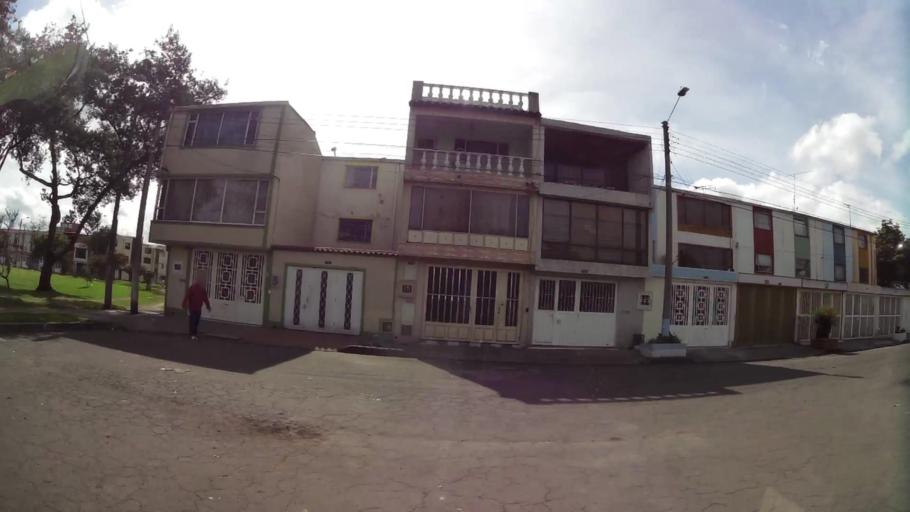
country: CO
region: Bogota D.C.
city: Bogota
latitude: 4.6440
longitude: -74.1356
